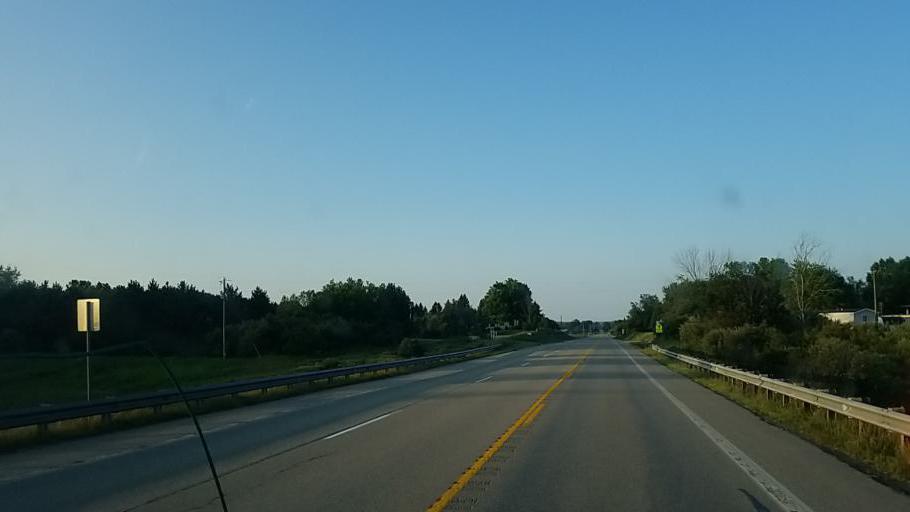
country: US
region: Michigan
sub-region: Isabella County
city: Lake Isabella
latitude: 43.6708
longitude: -85.1464
